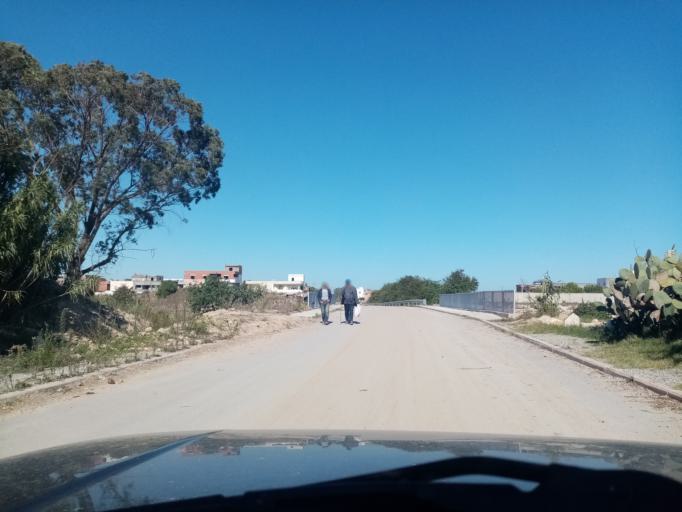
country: TN
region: Nabul
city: Bu `Urqub
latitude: 36.5795
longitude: 10.5704
